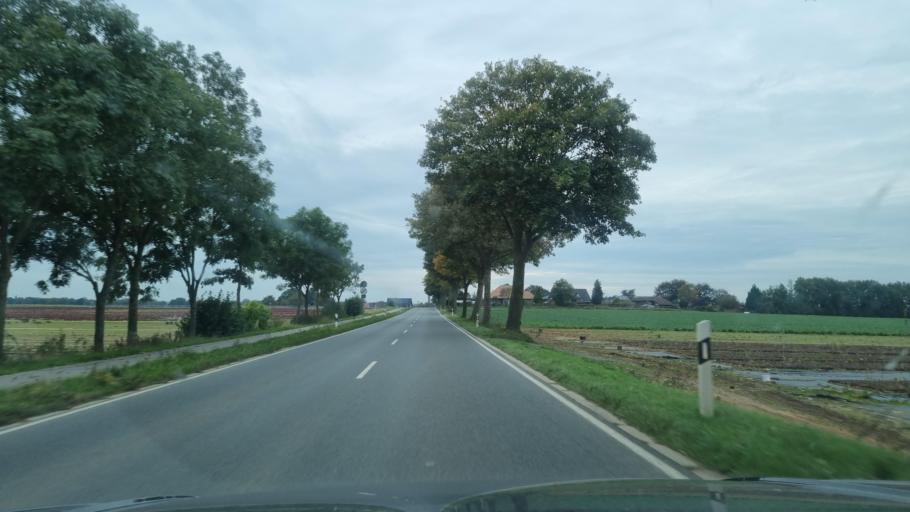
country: DE
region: North Rhine-Westphalia
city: Kalkar
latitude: 51.7257
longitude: 6.2862
